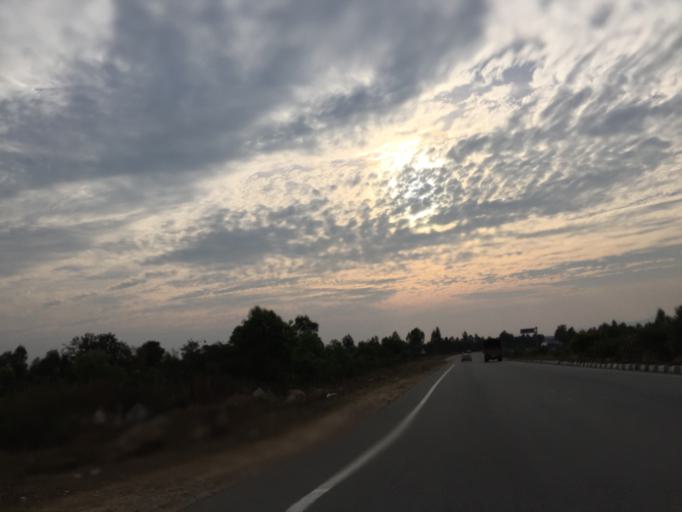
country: IN
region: Karnataka
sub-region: Kolar
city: Mulbagal
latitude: 13.1467
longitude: 78.2842
